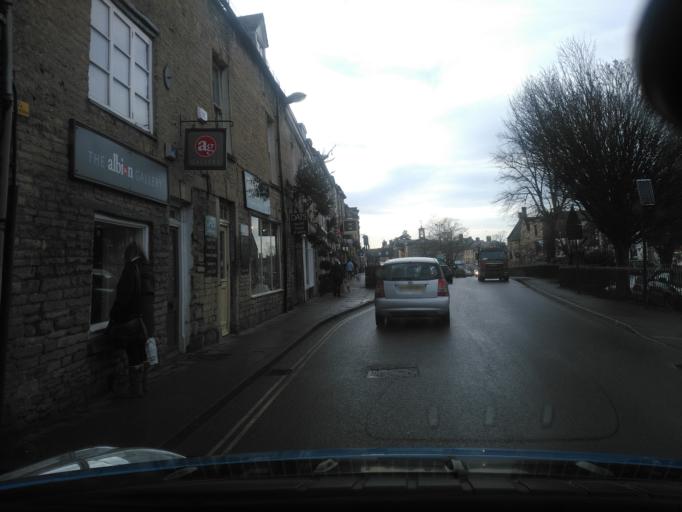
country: GB
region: England
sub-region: Oxfordshire
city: Chipping Norton
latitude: 51.9428
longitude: -1.5444
